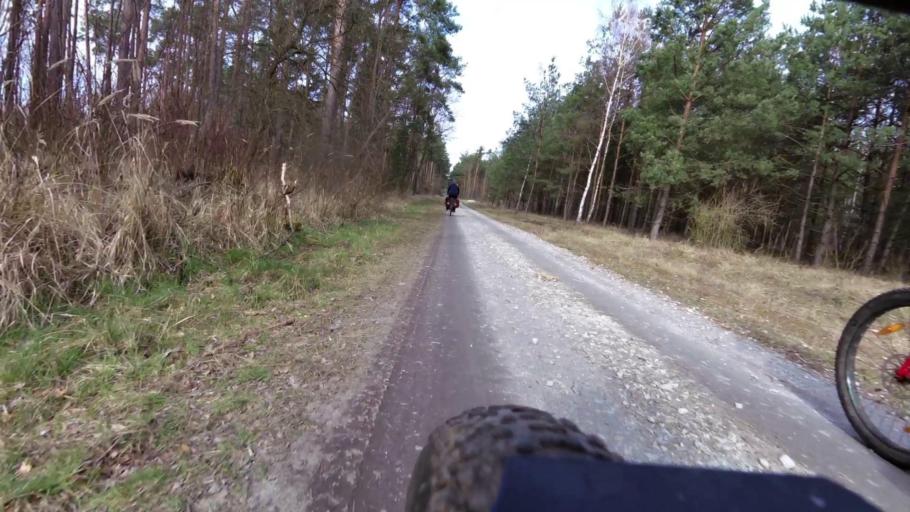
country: DE
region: Brandenburg
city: Wiesenau
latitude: 52.2838
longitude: 14.6469
